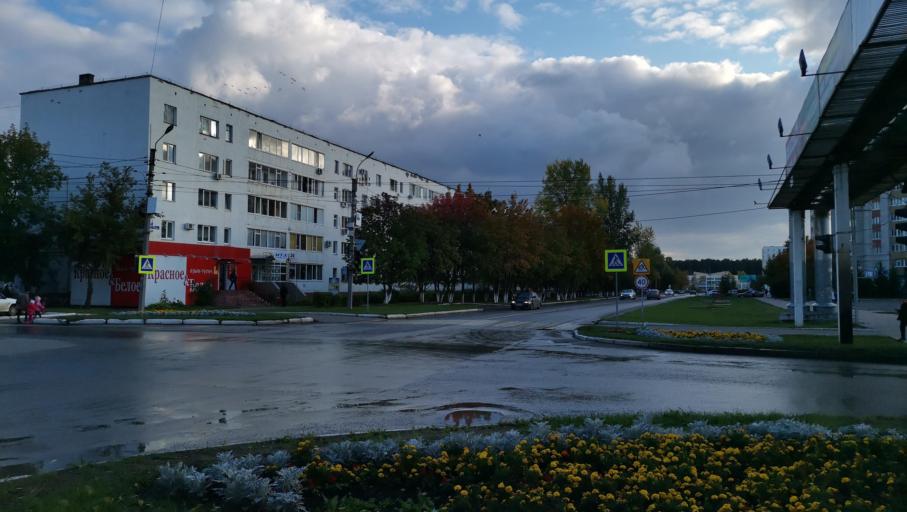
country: RU
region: Bashkortostan
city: Neftekamsk
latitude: 56.0981
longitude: 54.2363
